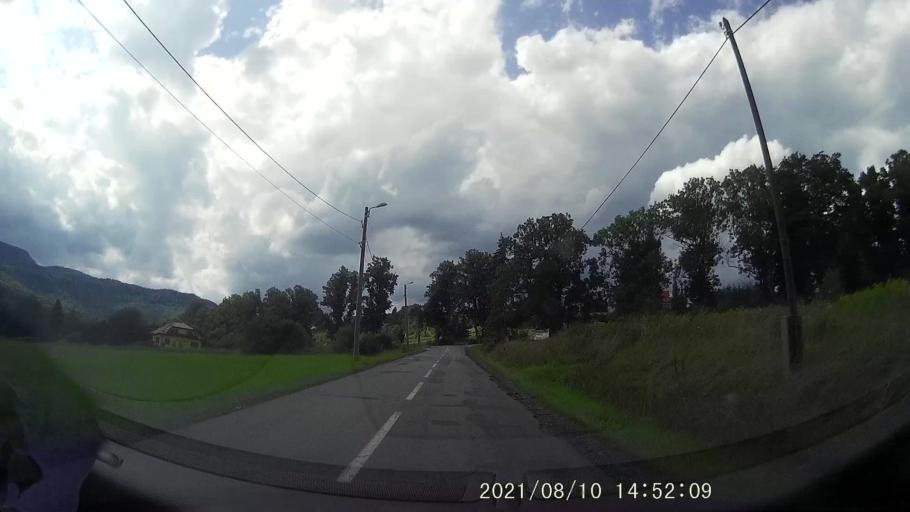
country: PL
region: Lower Silesian Voivodeship
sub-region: Powiat klodzki
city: Radkow
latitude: 50.4989
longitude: 16.3913
